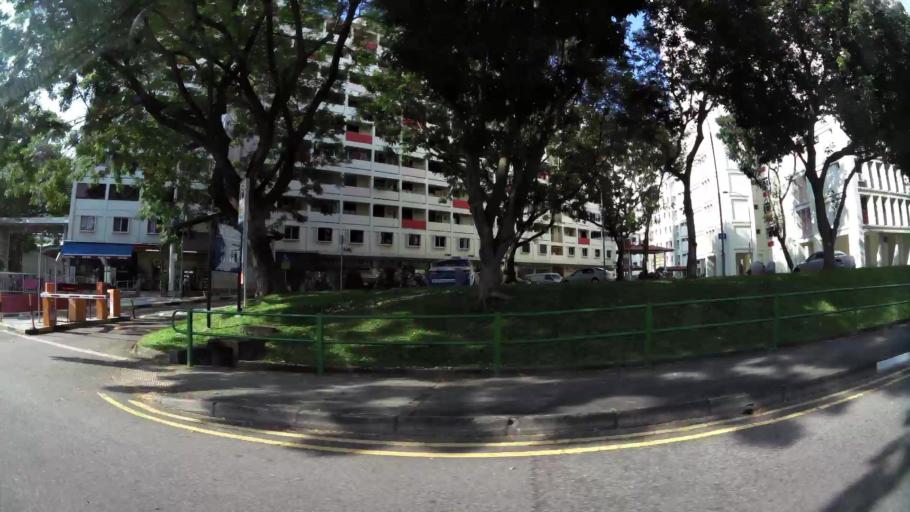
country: SG
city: Singapore
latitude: 1.3373
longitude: 103.8542
